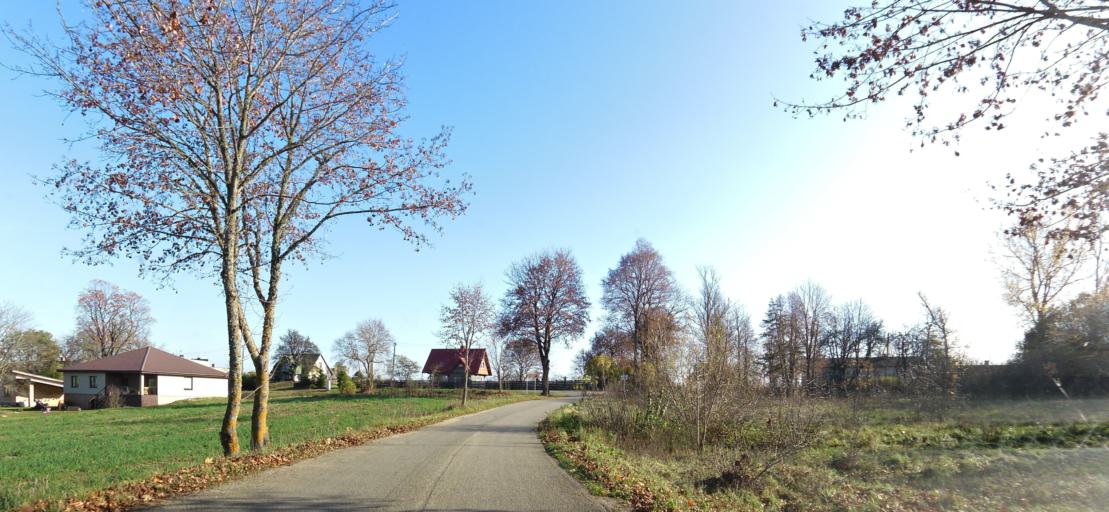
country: LT
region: Vilnius County
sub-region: Vilniaus Rajonas
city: Vievis
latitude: 54.6471
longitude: 24.7420
